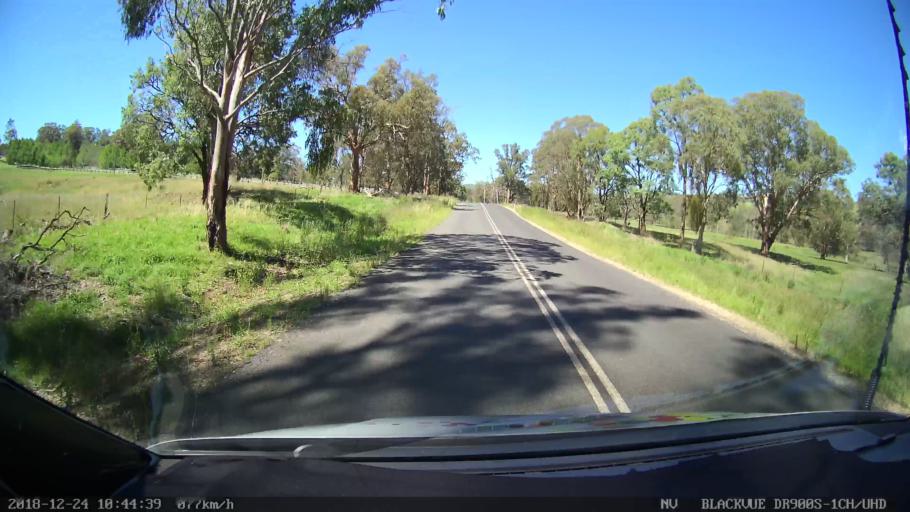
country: AU
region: New South Wales
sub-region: Upper Hunter Shire
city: Merriwa
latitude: -31.8952
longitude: 150.4423
